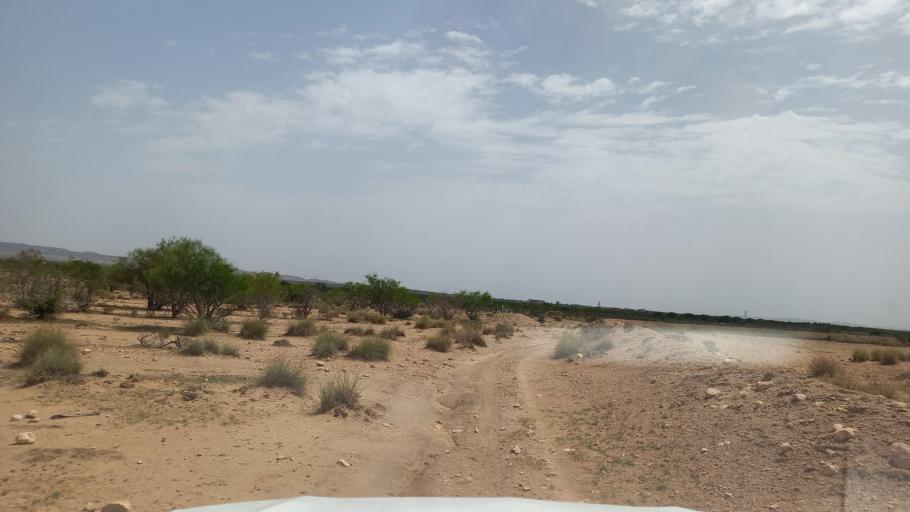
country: TN
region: Al Qasrayn
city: Kasserine
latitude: 35.2944
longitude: 9.0058
